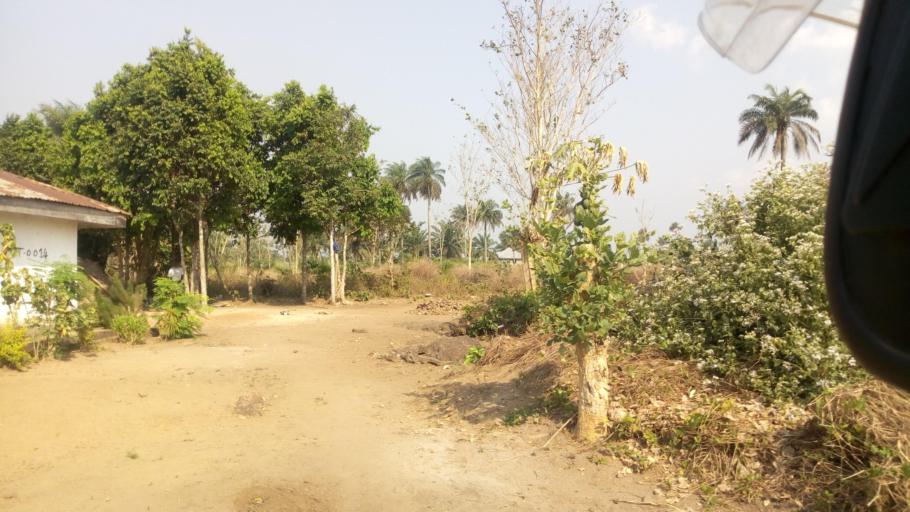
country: SL
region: Southern Province
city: Mogbwemo
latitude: 7.6158
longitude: -12.1757
